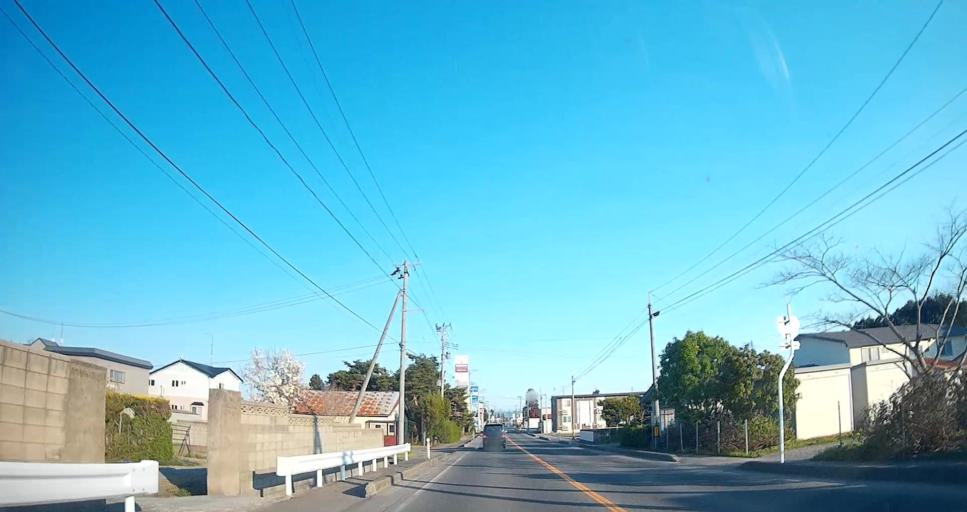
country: JP
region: Aomori
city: Mutsu
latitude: 41.2785
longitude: 141.2106
